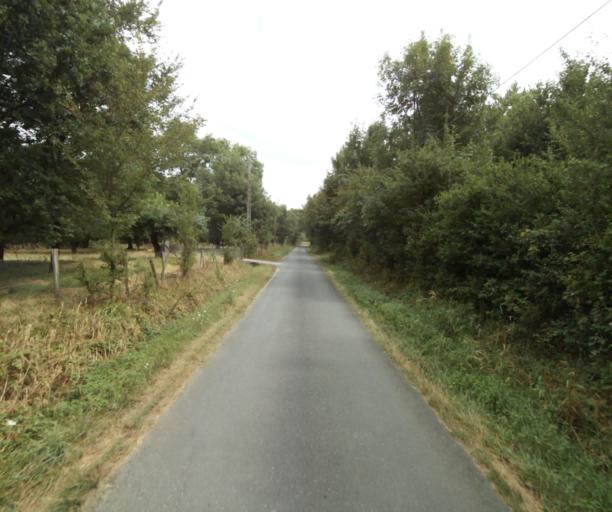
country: FR
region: Midi-Pyrenees
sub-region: Departement du Tarn
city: Soreze
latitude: 43.4642
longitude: 2.0562
